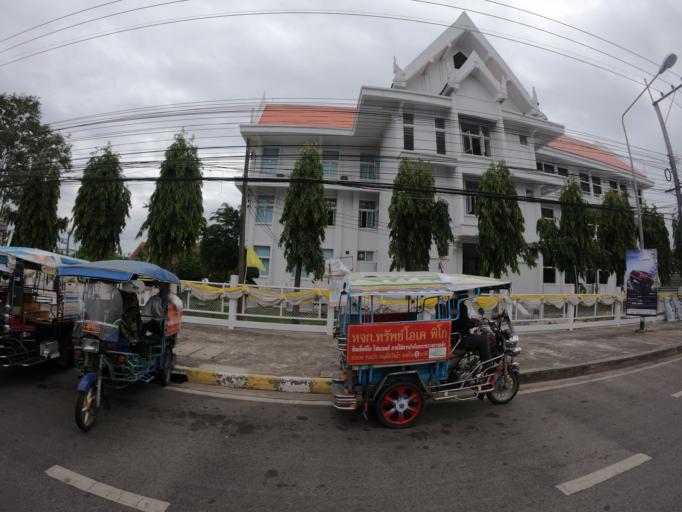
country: TH
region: Roi Et
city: Roi Et
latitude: 16.0529
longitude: 103.6532
